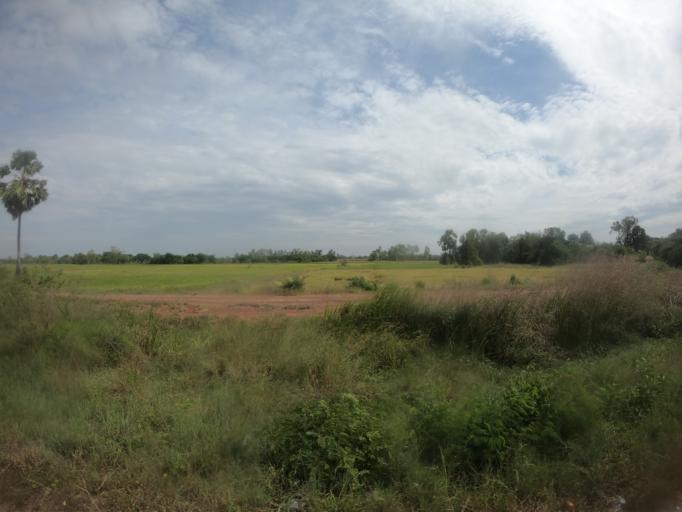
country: TH
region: Maha Sarakham
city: Chiang Yuen
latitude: 16.3892
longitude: 103.1017
